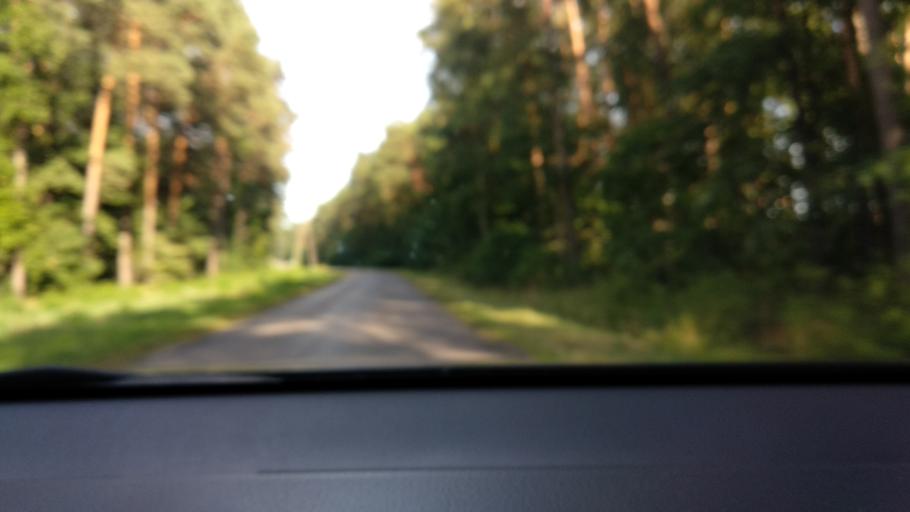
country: PL
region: Masovian Voivodeship
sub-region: Powiat pultuski
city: Pultusk
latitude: 52.7128
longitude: 21.1586
